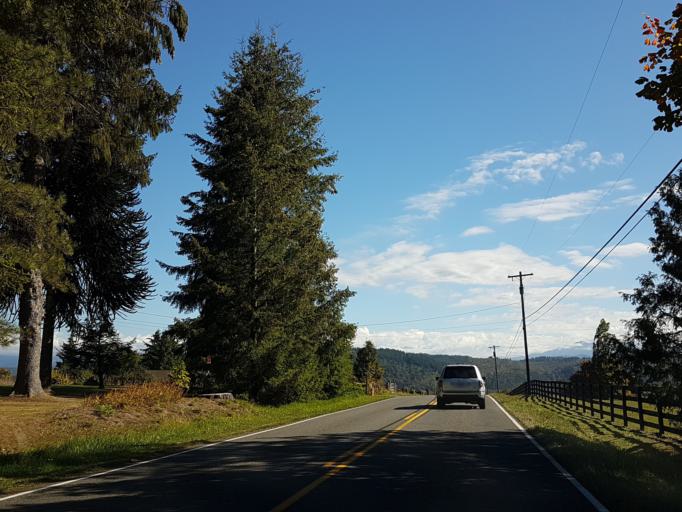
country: US
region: Washington
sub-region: Snohomish County
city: Cathcart
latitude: 47.8483
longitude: -122.1079
